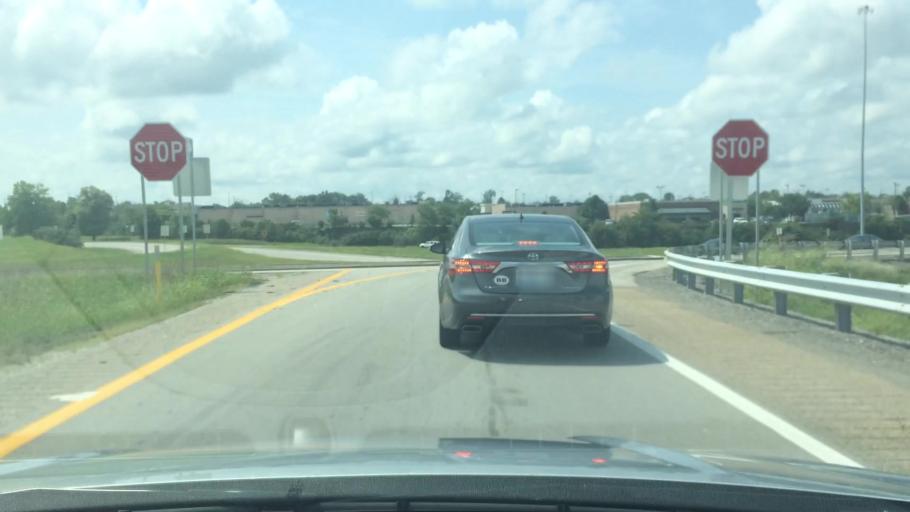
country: US
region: Kentucky
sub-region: Franklin County
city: Frankfort
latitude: 38.1602
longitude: -84.8933
